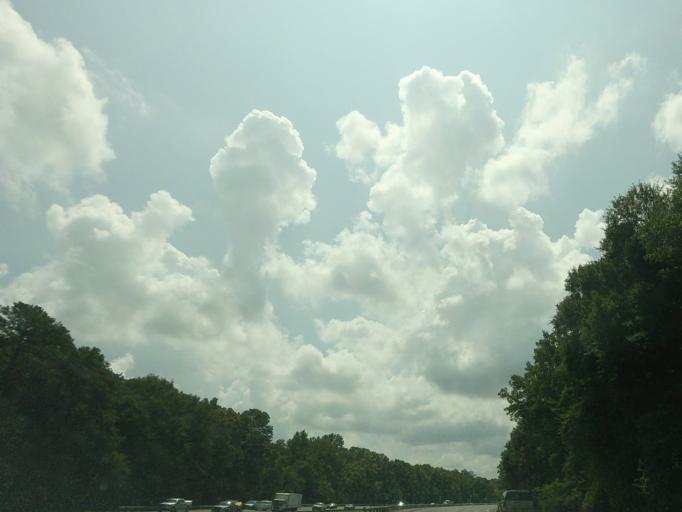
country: US
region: Georgia
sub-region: Bibb County
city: West Point
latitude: 32.7746
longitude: -83.7121
